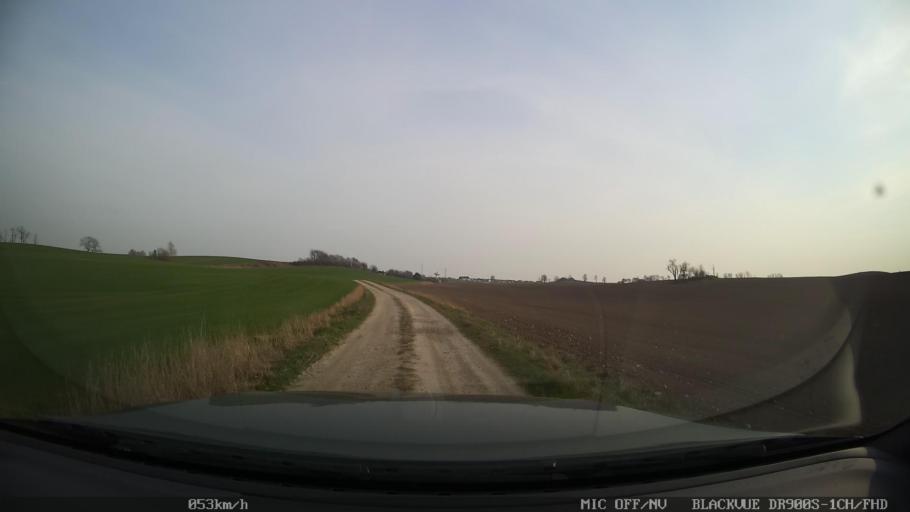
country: SE
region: Skane
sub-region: Ystads Kommun
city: Ystad
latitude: 55.4563
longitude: 13.7913
